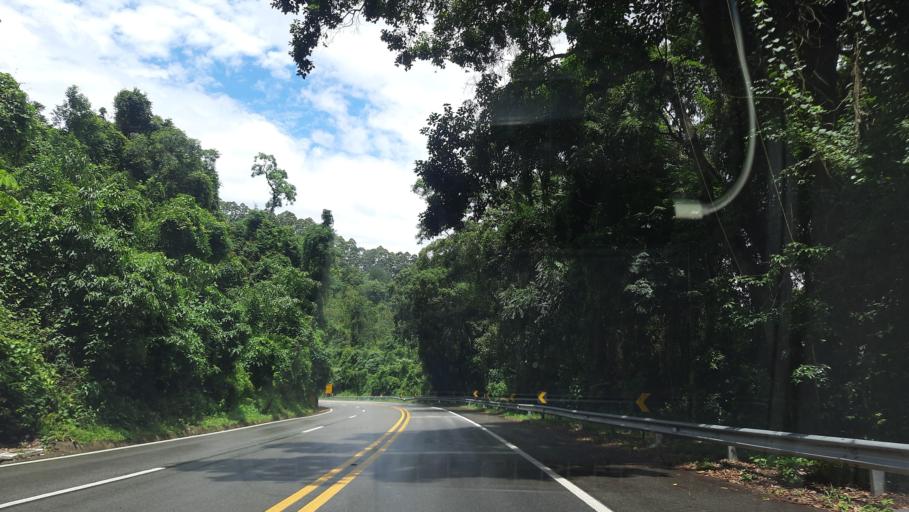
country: BR
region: Minas Gerais
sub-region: Pocos De Caldas
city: Pocos de Caldas
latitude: -21.8437
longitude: -46.6958
